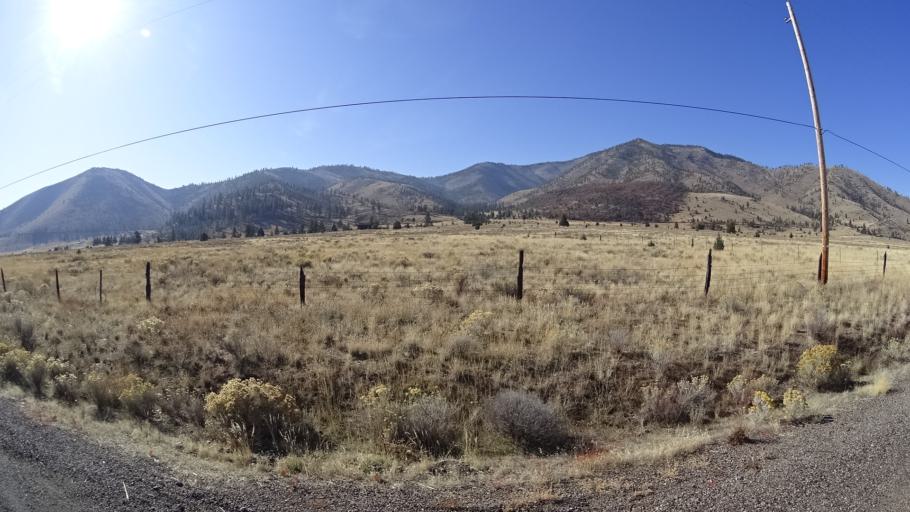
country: US
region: California
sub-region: Siskiyou County
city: Weed
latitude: 41.4766
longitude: -122.4866
